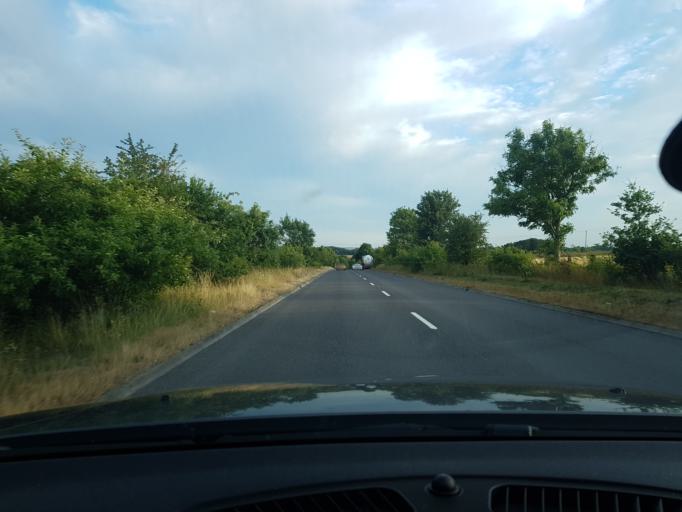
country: GB
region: England
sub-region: West Berkshire
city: Hungerford
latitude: 51.4511
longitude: -1.4836
